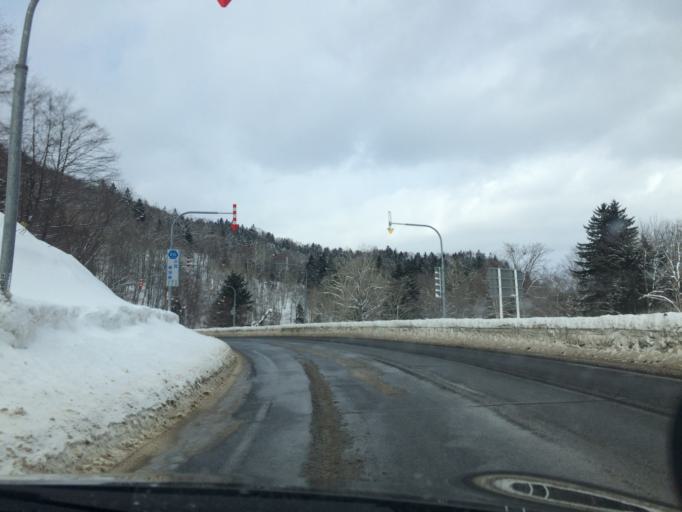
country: JP
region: Hokkaido
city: Shimo-furano
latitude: 42.9263
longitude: 142.3743
